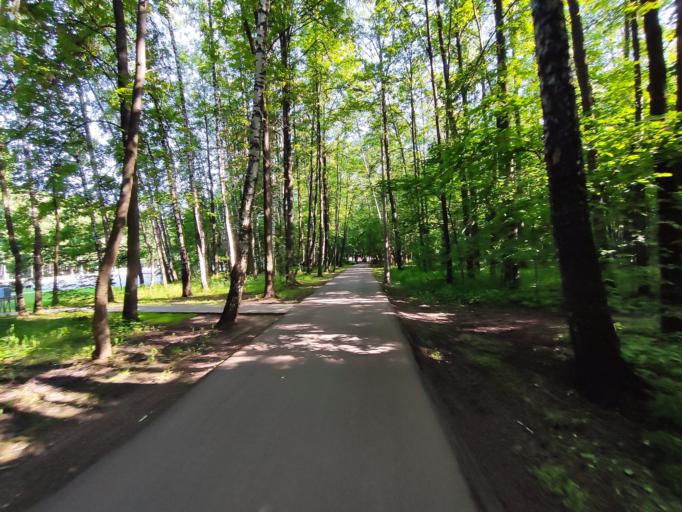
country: RU
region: Moscow
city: Metrogorodok
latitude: 55.7839
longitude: 37.7528
